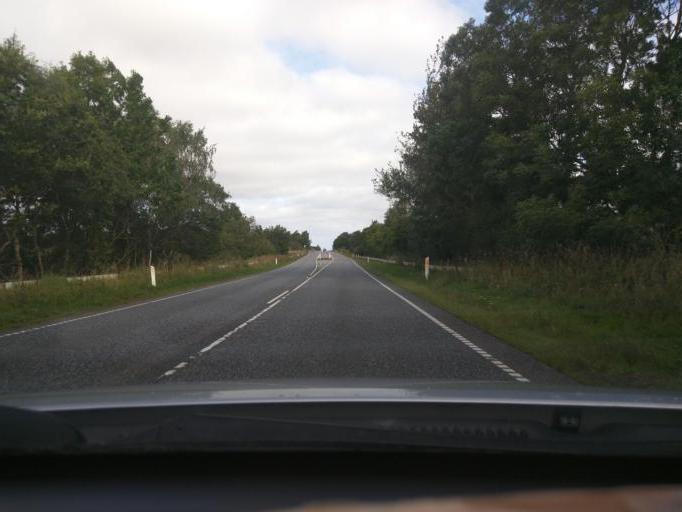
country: DK
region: Central Jutland
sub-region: Viborg Kommune
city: Viborg
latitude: 56.3864
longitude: 9.3796
